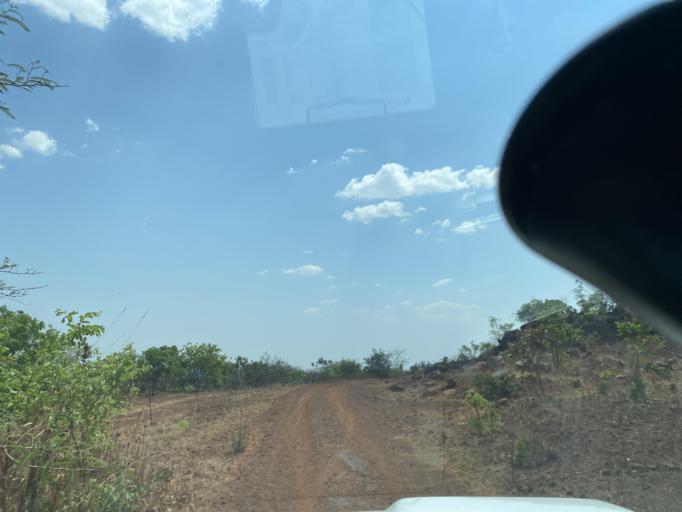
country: ZM
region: Lusaka
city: Lusaka
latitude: -15.4978
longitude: 27.9635
